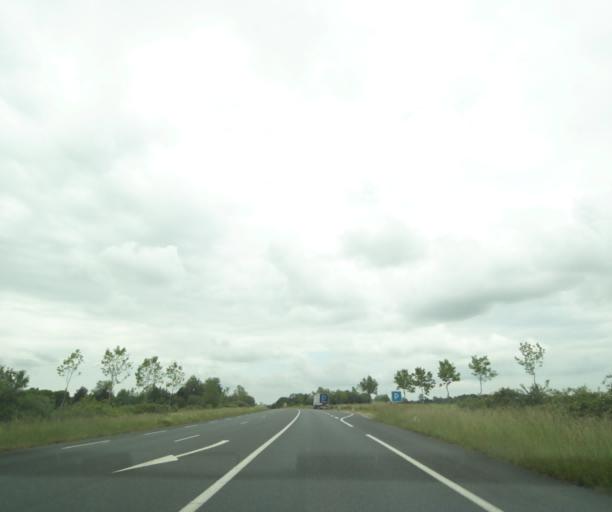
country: FR
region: Poitou-Charentes
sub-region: Departement des Deux-Sevres
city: Saint-Varent
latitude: 46.9055
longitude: -0.1912
